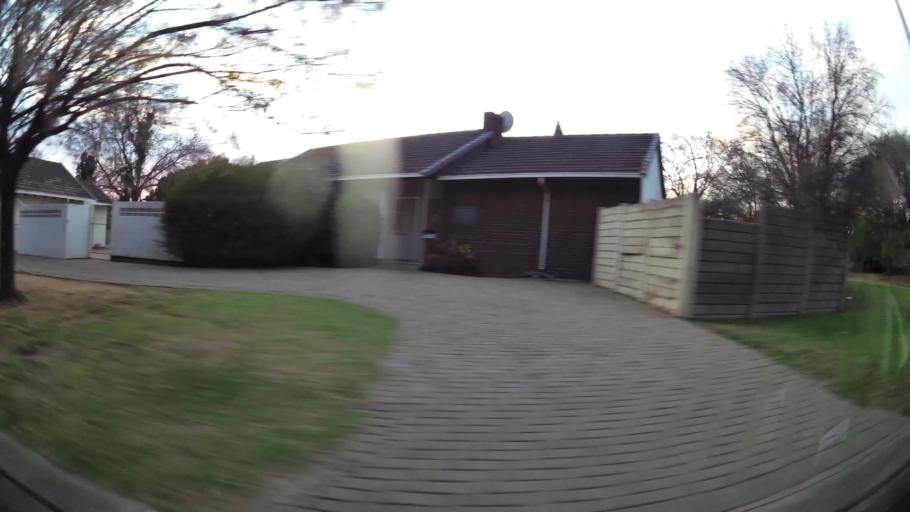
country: ZA
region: Gauteng
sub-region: Ekurhuleni Metropolitan Municipality
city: Benoni
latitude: -26.1697
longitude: 28.3044
